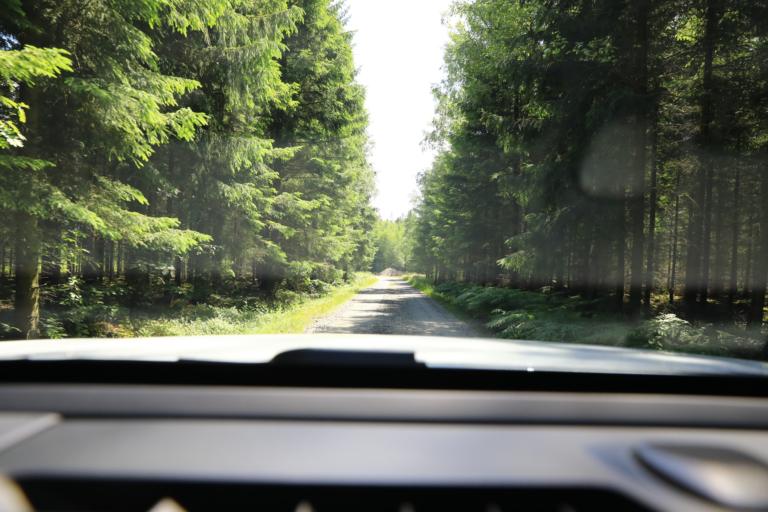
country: SE
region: Halland
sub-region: Varbergs Kommun
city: Tvaaker
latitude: 57.0971
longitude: 12.4832
